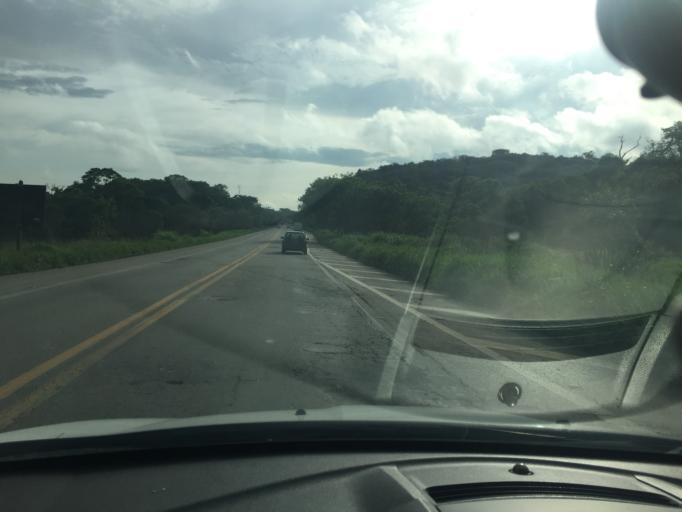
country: BR
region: Sao Paulo
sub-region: Campo Limpo Paulista
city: Campo Limpo Paulista
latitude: -23.1950
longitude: -46.7923
